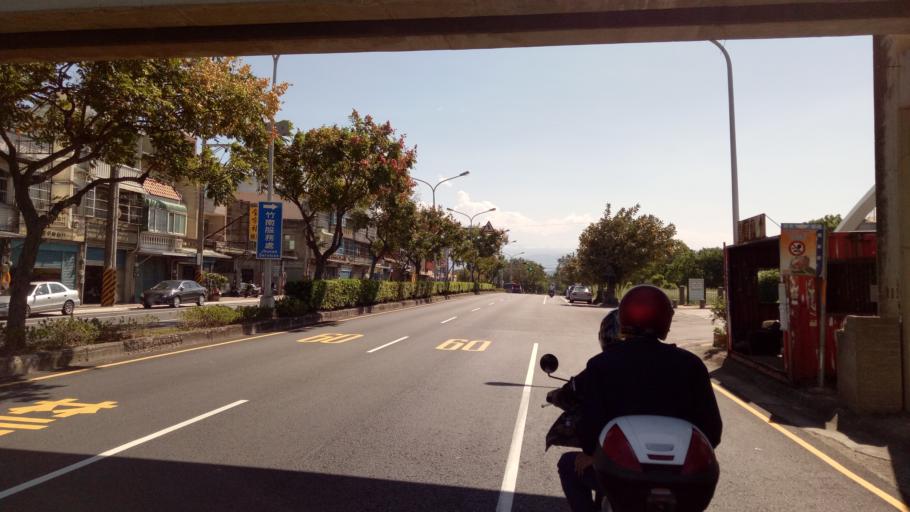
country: TW
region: Taiwan
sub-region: Hsinchu
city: Hsinchu
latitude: 24.7077
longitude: 120.9250
